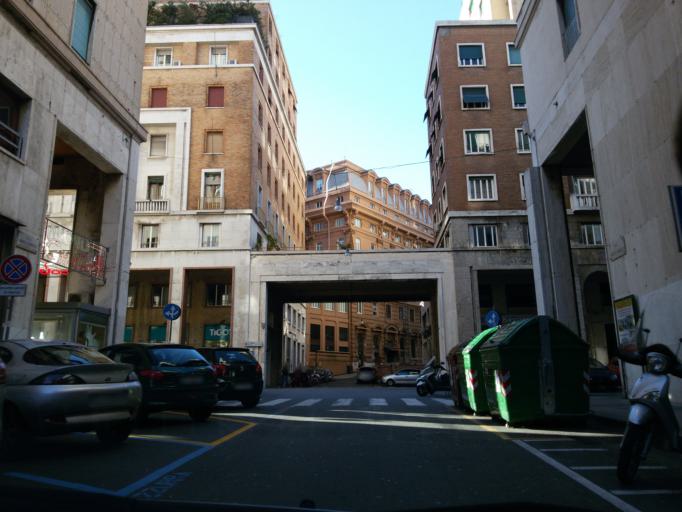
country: IT
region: Liguria
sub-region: Provincia di Genova
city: San Teodoro
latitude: 44.4059
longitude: 8.9365
